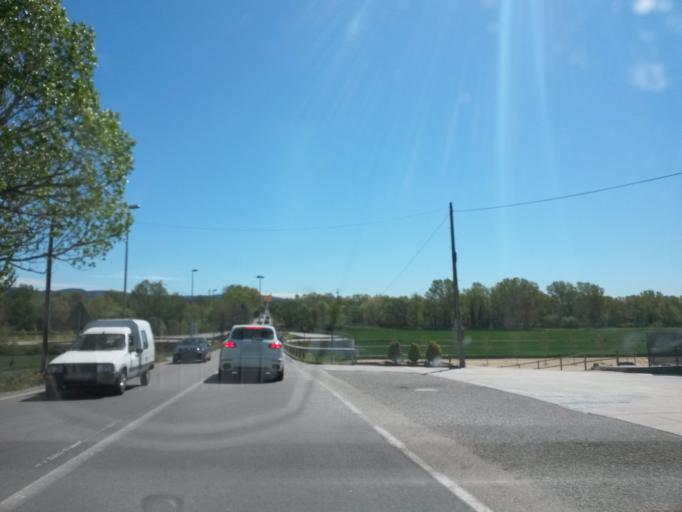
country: ES
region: Catalonia
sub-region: Provincia de Girona
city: Riudellots de la Selva
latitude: 41.8987
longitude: 2.8133
